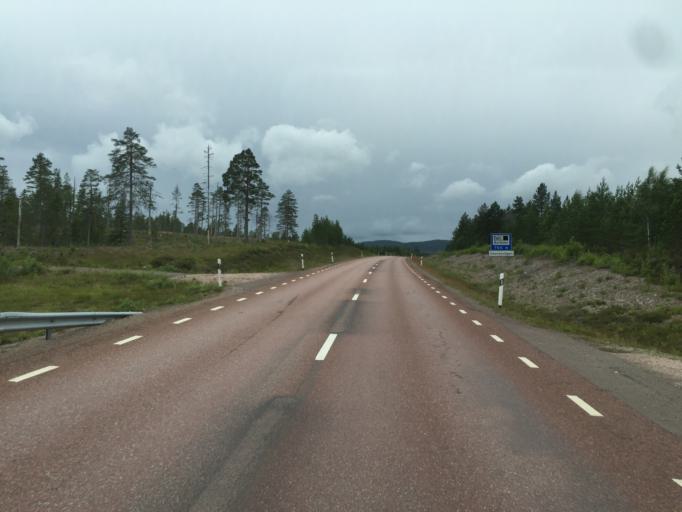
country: SE
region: Dalarna
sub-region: Malung-Saelens kommun
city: Malung
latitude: 60.6538
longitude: 13.6800
